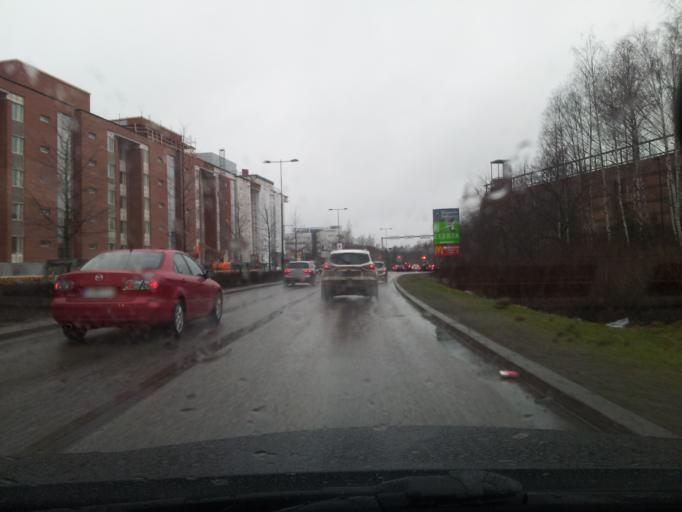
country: FI
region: Uusimaa
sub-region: Helsinki
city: Koukkuniemi
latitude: 60.1656
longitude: 24.7356
